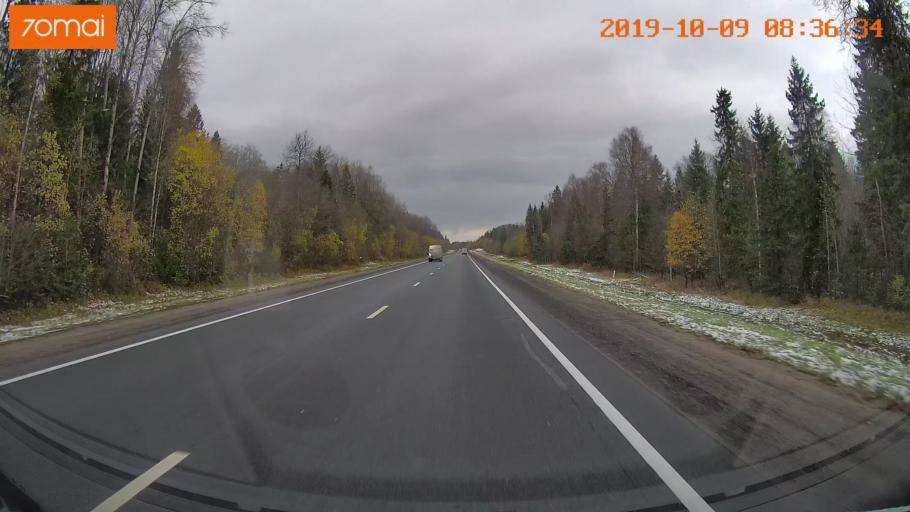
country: RU
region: Vologda
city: Gryazovets
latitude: 58.9285
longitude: 40.1761
